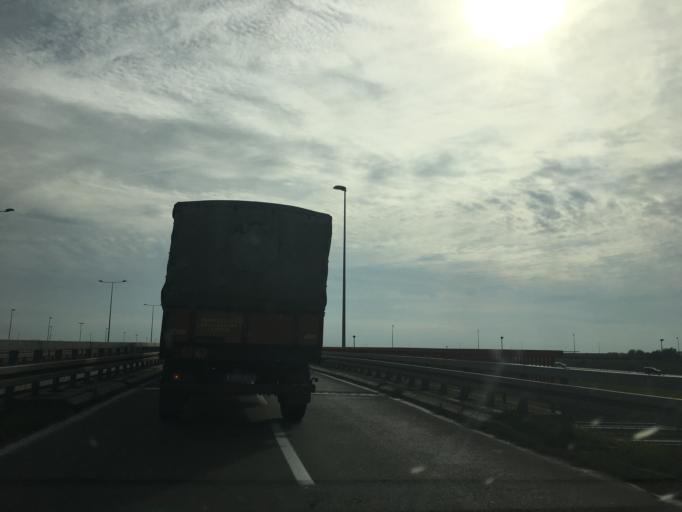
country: RS
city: Dobanovci
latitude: 44.8365
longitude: 20.2503
